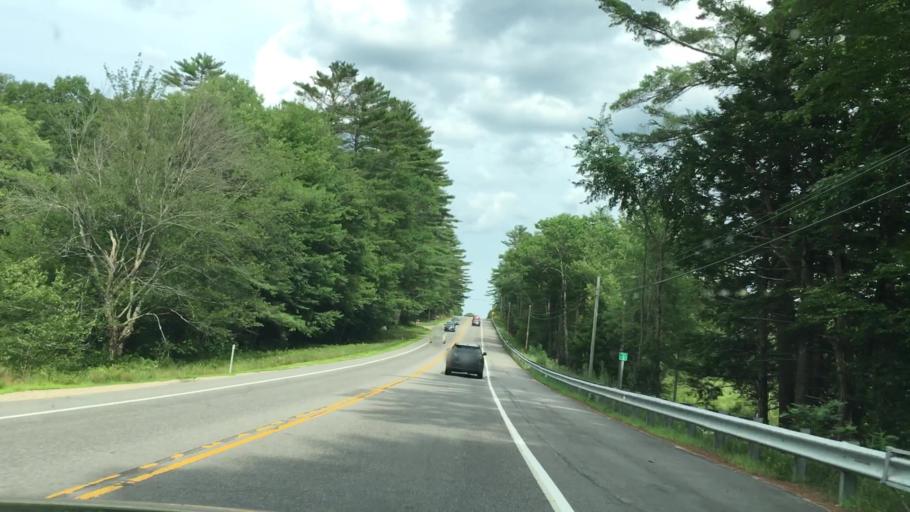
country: US
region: New Hampshire
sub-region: Grafton County
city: Ashland
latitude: 43.6230
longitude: -71.6114
